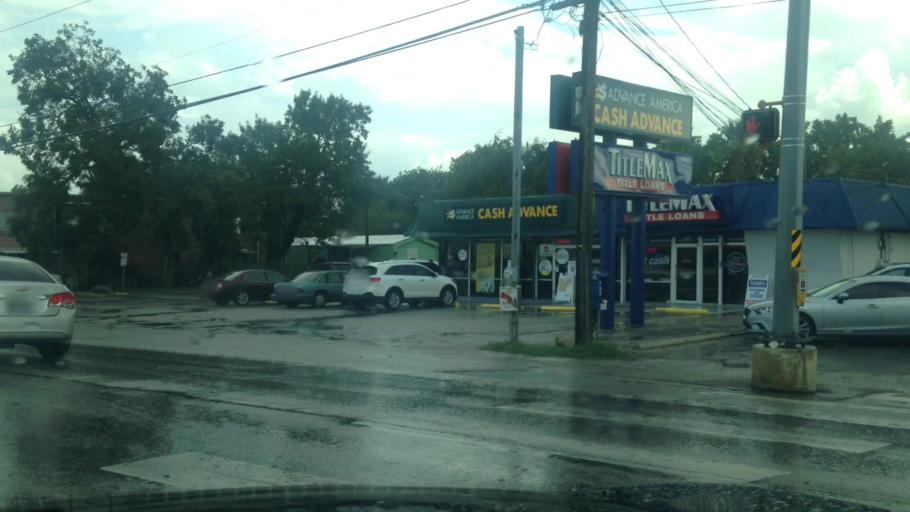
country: US
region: Texas
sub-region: Bexar County
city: Balcones Heights
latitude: 29.4876
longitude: -98.5490
